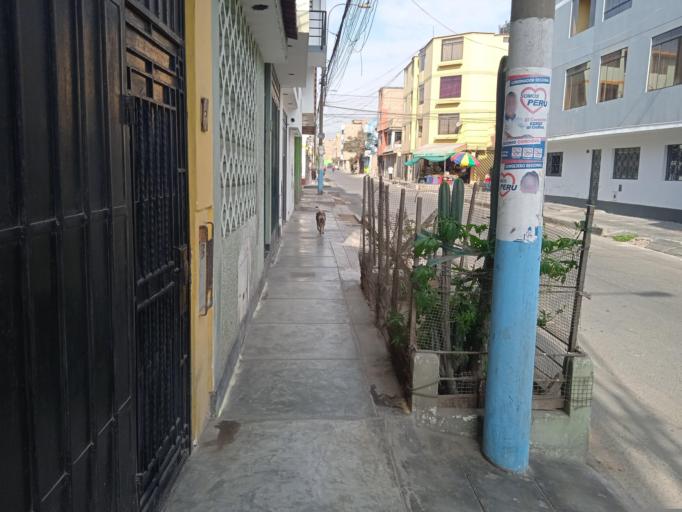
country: PE
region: Callao
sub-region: Callao
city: Callao
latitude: -12.0101
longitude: -77.0959
